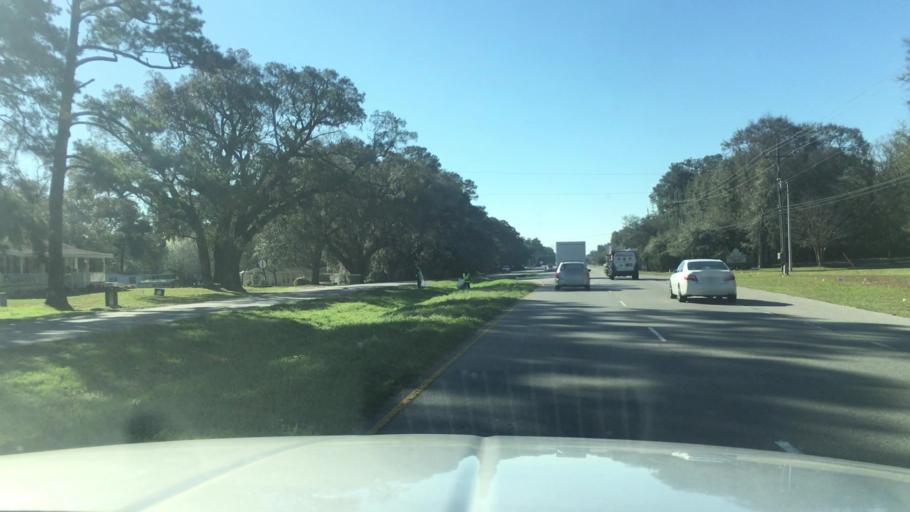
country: US
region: North Carolina
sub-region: New Hanover County
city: Sea Breeze
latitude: 34.0938
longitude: -77.8975
